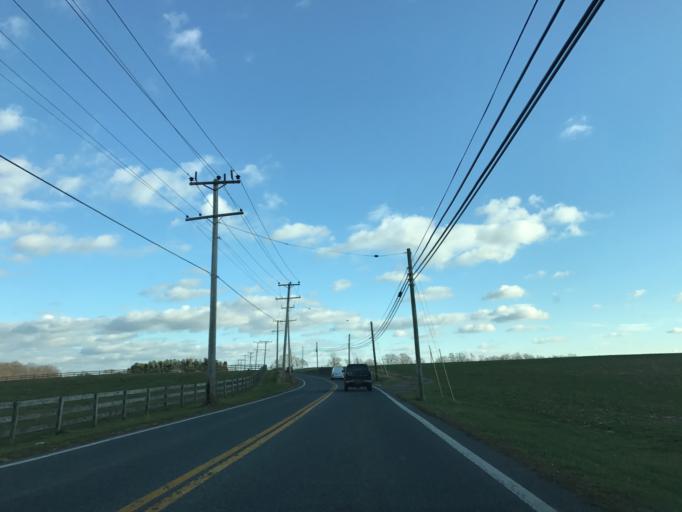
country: US
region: Maryland
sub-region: Harford County
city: Jarrettsville
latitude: 39.6148
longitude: -76.5401
